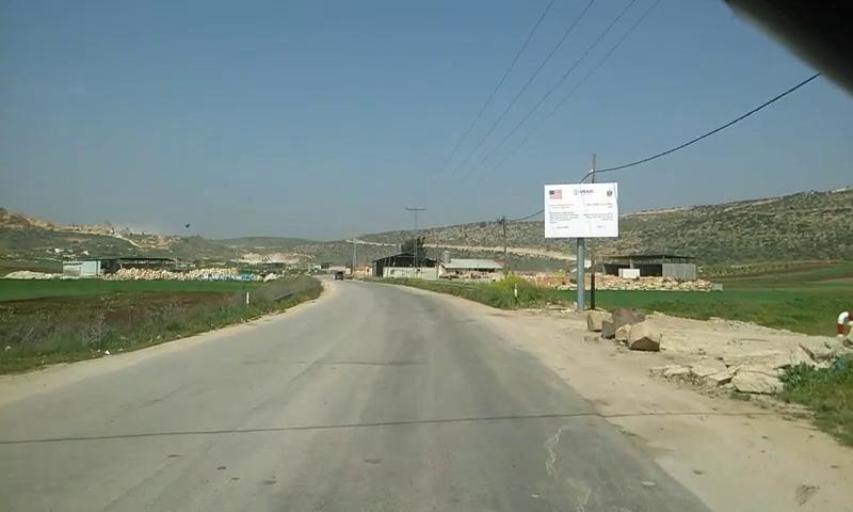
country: PS
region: West Bank
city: Az Zababidah
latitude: 32.3950
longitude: 35.3205
